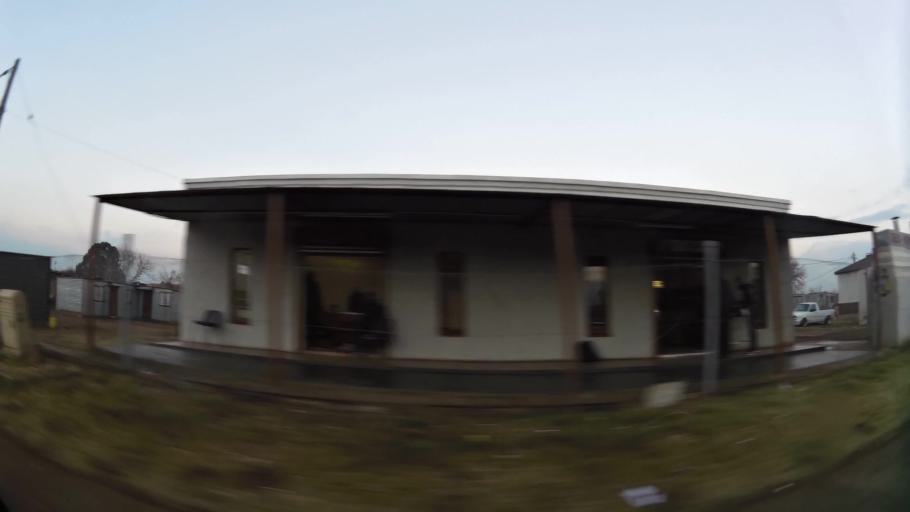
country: ZA
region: Gauteng
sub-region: City of Johannesburg Metropolitan Municipality
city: Orange Farm
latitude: -26.5490
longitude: 27.8489
